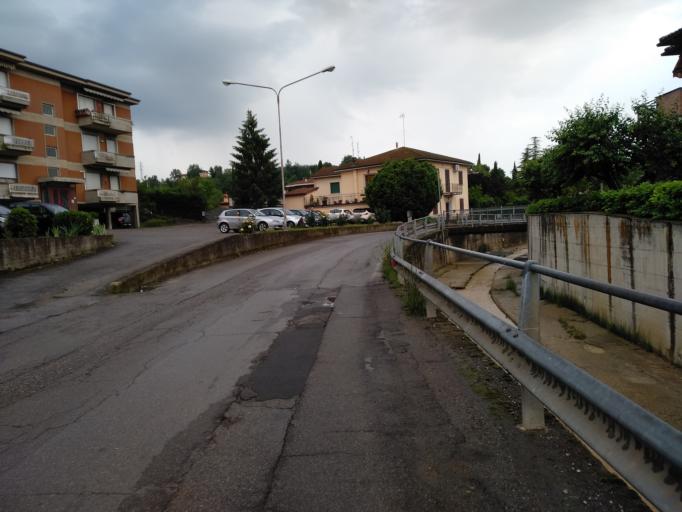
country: IT
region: Tuscany
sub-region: Province of Arezzo
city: San Giovanni Valdarno
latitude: 43.5608
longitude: 11.5282
